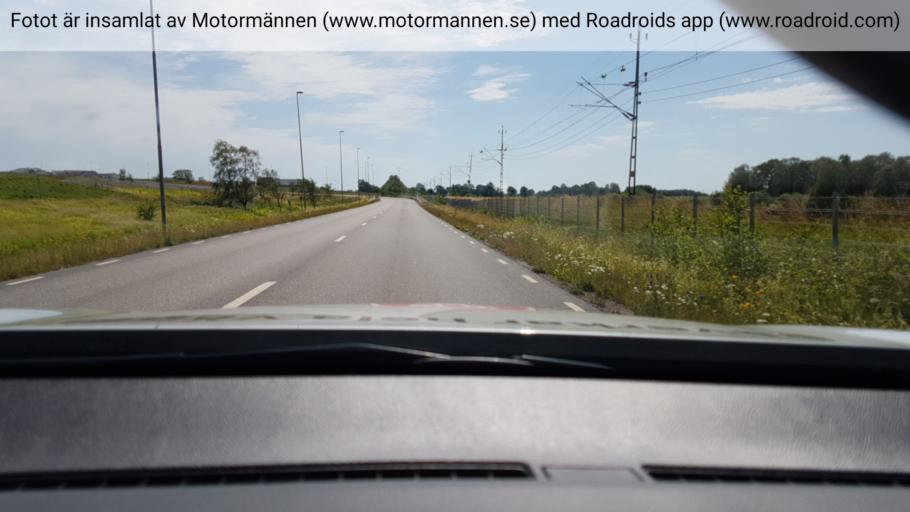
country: SE
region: Vaestra Goetaland
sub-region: Falkopings Kommun
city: Falkoeping
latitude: 58.1553
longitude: 13.5458
